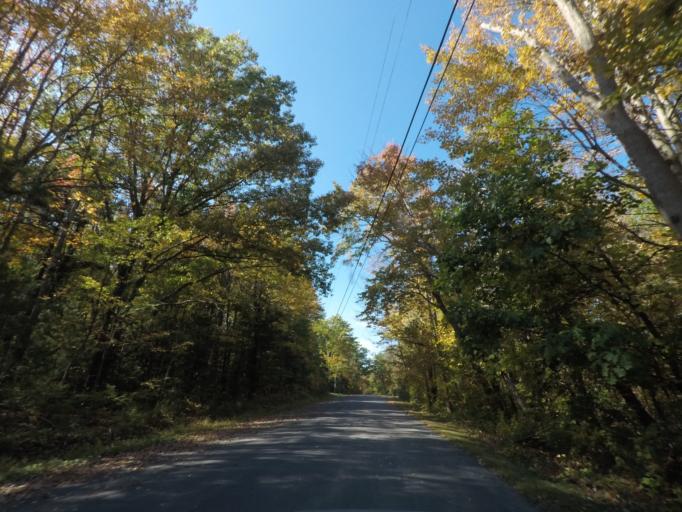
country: US
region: New York
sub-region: Rensselaer County
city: Averill Park
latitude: 42.6471
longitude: -73.5521
